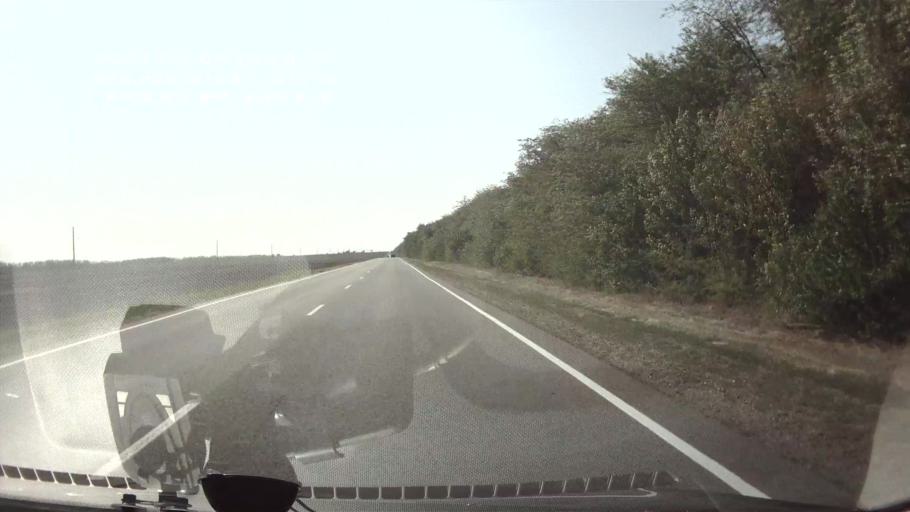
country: RU
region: Krasnodarskiy
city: Novopokrovskaya
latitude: 45.8955
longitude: 40.7210
